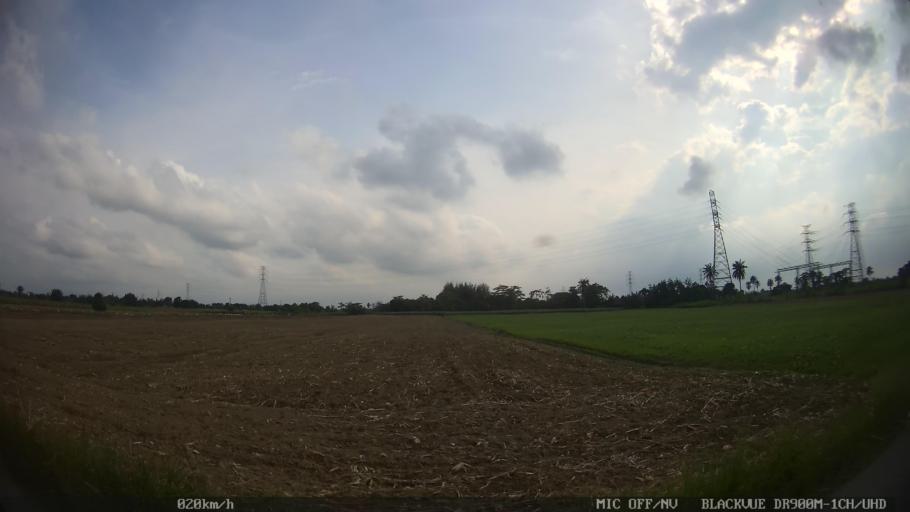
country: ID
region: North Sumatra
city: Percut
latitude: 3.5663
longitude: 98.7837
